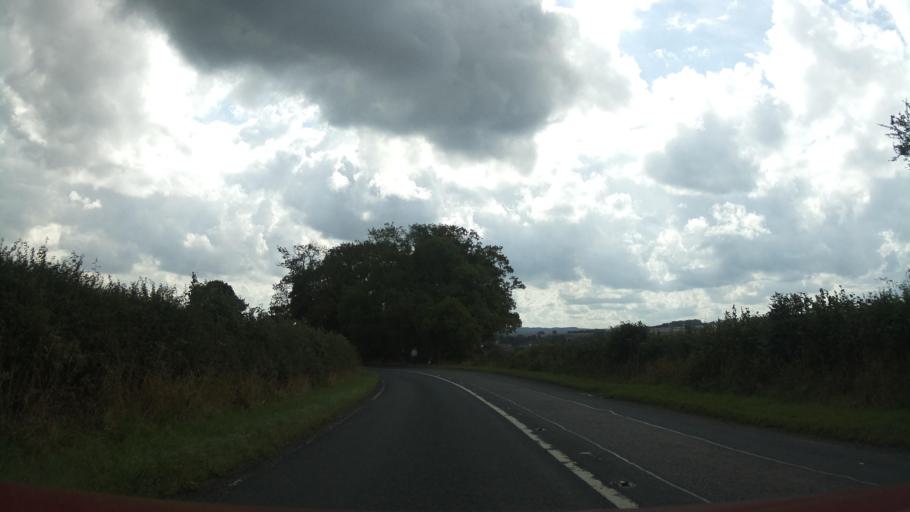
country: GB
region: England
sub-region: North Yorkshire
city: Catterick Garrison
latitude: 54.4302
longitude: -1.6808
